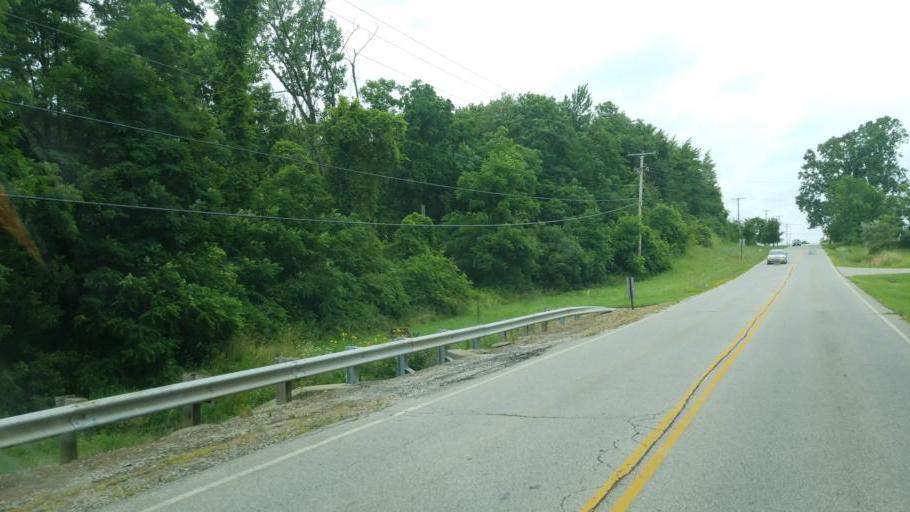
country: US
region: Ohio
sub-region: Richland County
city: Ontario
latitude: 40.7824
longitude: -82.5708
